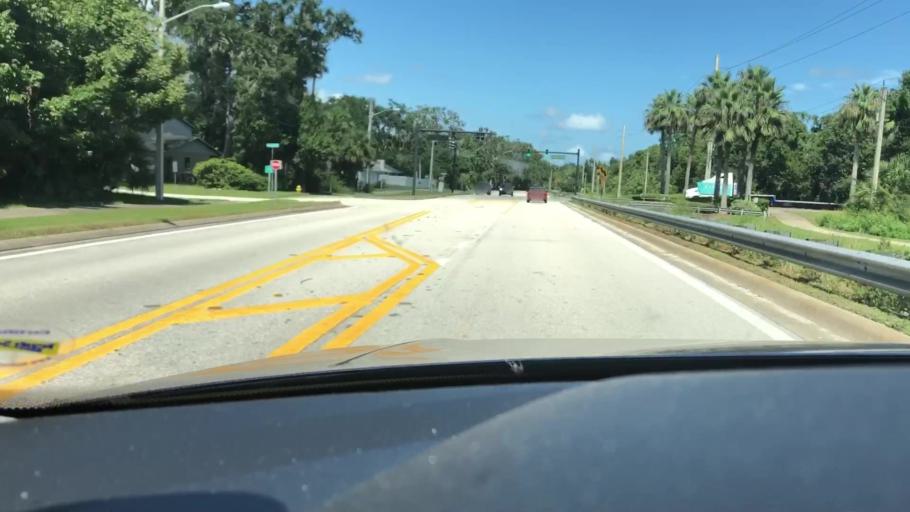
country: US
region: Florida
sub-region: Volusia County
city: Port Orange
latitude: 29.1304
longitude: -80.9933
